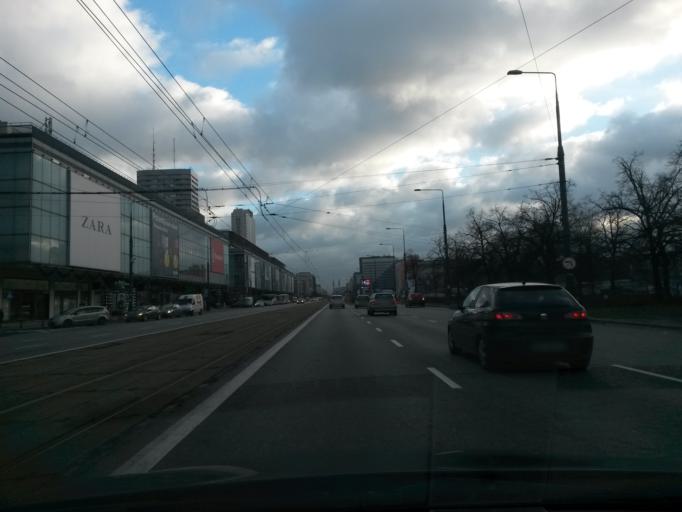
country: PL
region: Masovian Voivodeship
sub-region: Warszawa
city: Warsaw
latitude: 52.2340
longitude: 21.0092
